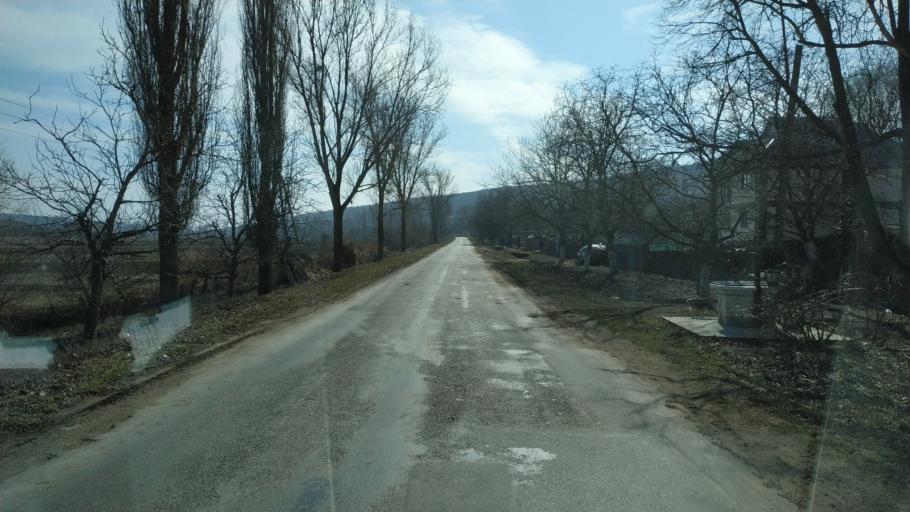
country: MD
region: Nisporeni
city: Nisporeni
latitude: 47.1529
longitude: 28.1079
